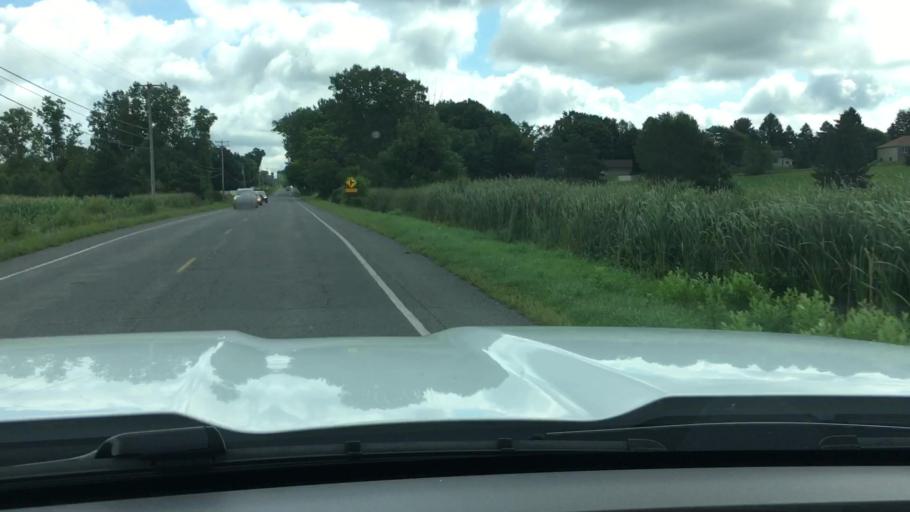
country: US
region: Michigan
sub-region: Eaton County
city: Dimondale
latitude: 42.5821
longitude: -84.5887
